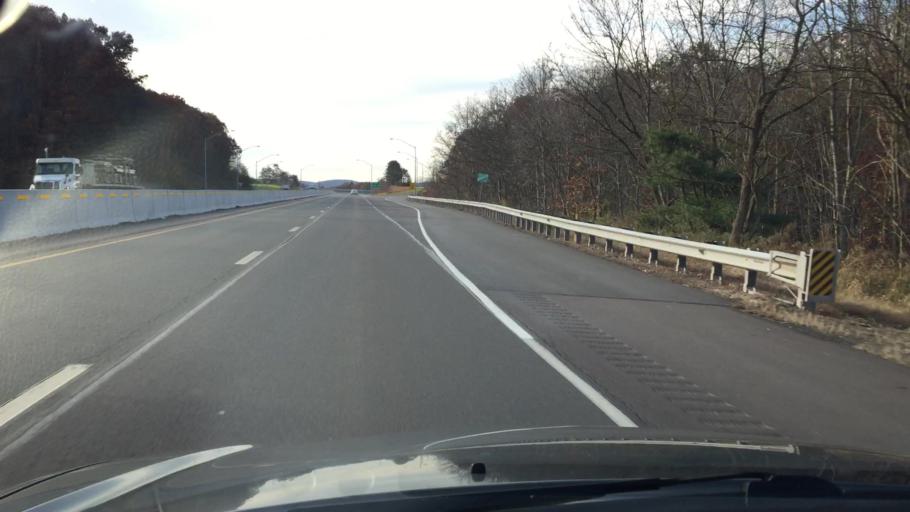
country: US
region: Pennsylvania
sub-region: Luzerne County
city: Plymouth
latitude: 41.2033
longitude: -75.9393
